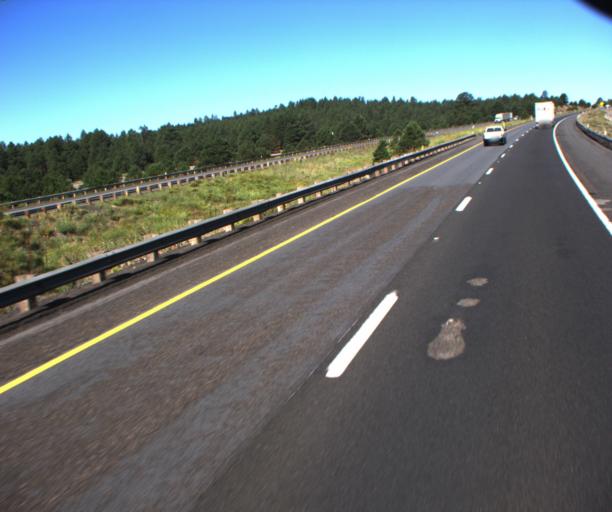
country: US
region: Arizona
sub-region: Coconino County
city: Parks
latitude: 35.2477
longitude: -111.8885
